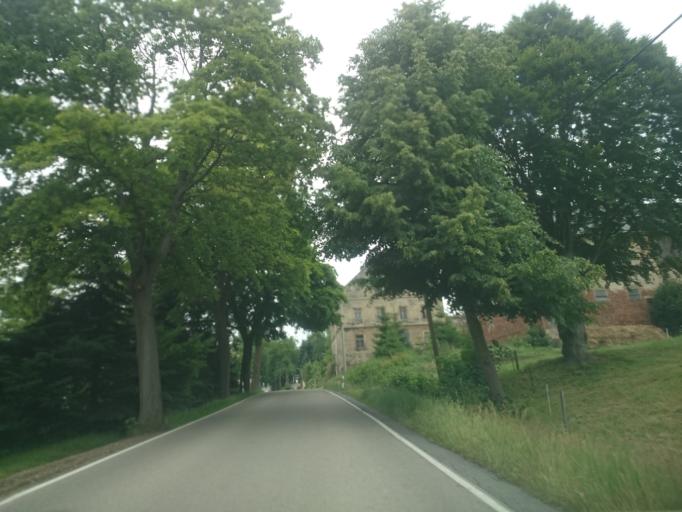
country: DE
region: Saxony
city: Eppendorf
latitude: 50.8127
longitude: 13.2558
